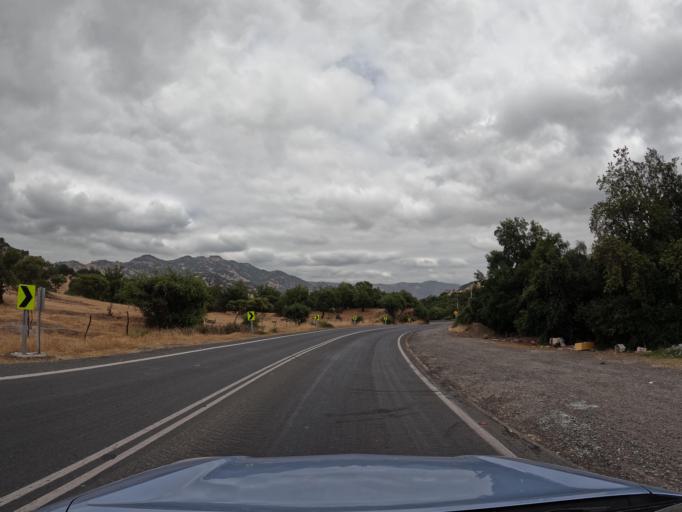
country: CL
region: Maule
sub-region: Provincia de Curico
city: Teno
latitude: -34.8171
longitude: -71.1955
